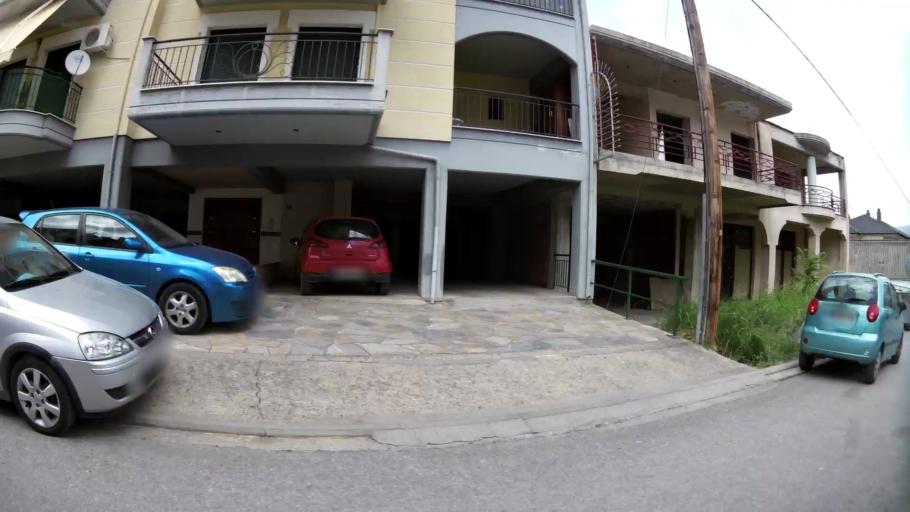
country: GR
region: Central Macedonia
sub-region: Nomos Imathias
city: Veroia
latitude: 40.5171
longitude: 22.2086
